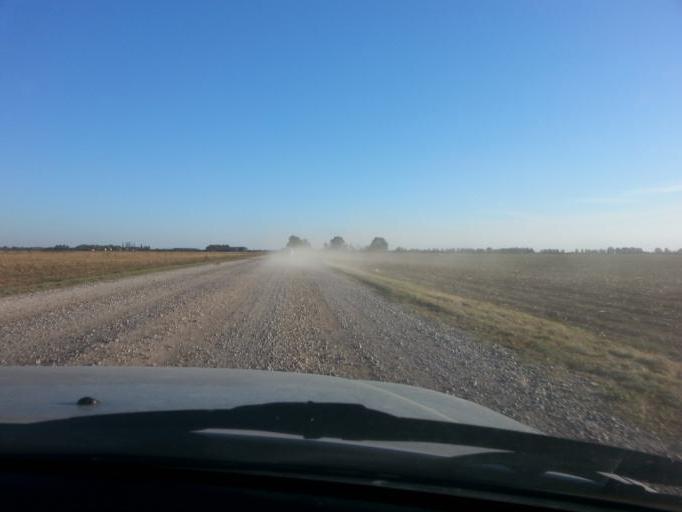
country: LV
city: Tervete
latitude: 56.6105
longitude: 23.4797
